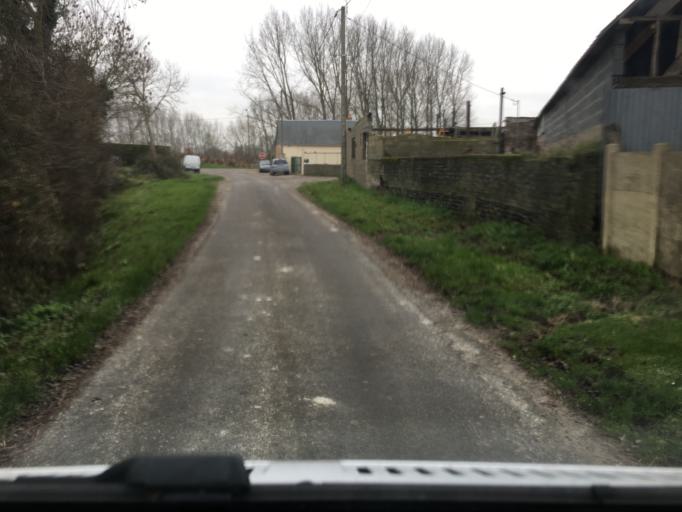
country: FR
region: Picardie
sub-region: Departement de la Somme
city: Pende
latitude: 50.1730
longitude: 1.5456
